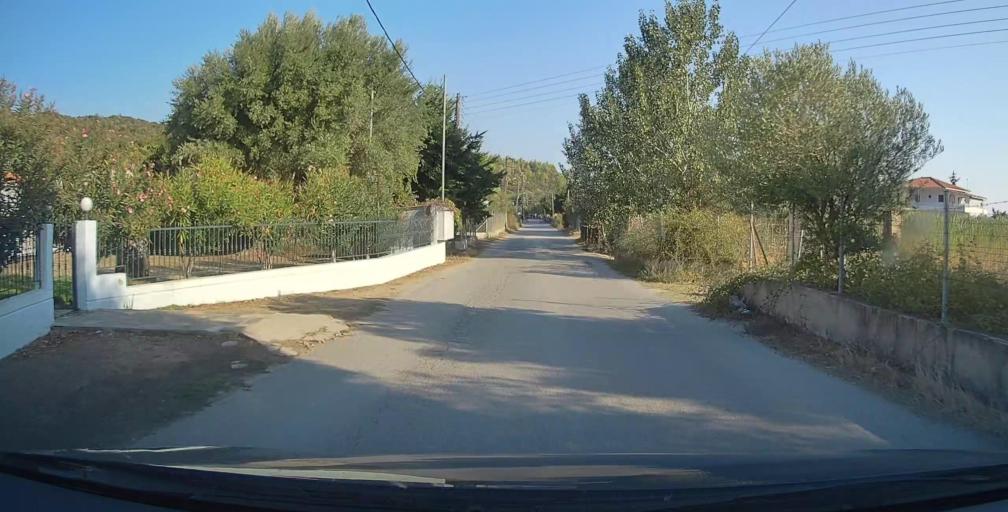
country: GR
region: Central Macedonia
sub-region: Nomos Chalkidikis
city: Sykia
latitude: 39.9965
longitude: 23.8899
